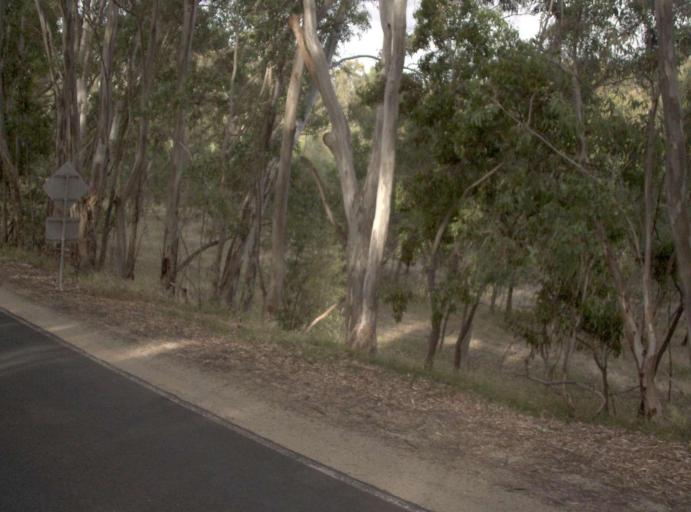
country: AU
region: Victoria
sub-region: Wellington
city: Sale
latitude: -37.9241
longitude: 146.9967
